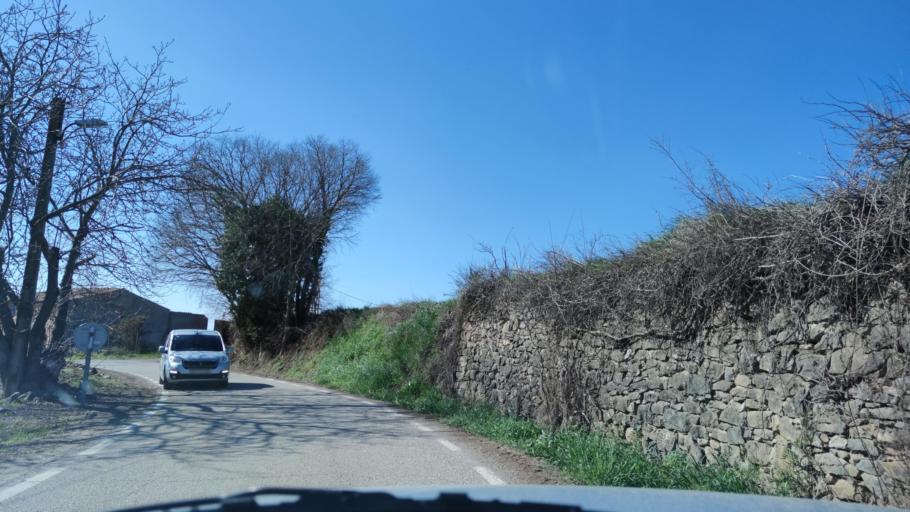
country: ES
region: Catalonia
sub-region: Provincia de Lleida
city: Artesa de Segre
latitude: 41.9931
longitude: 1.0228
